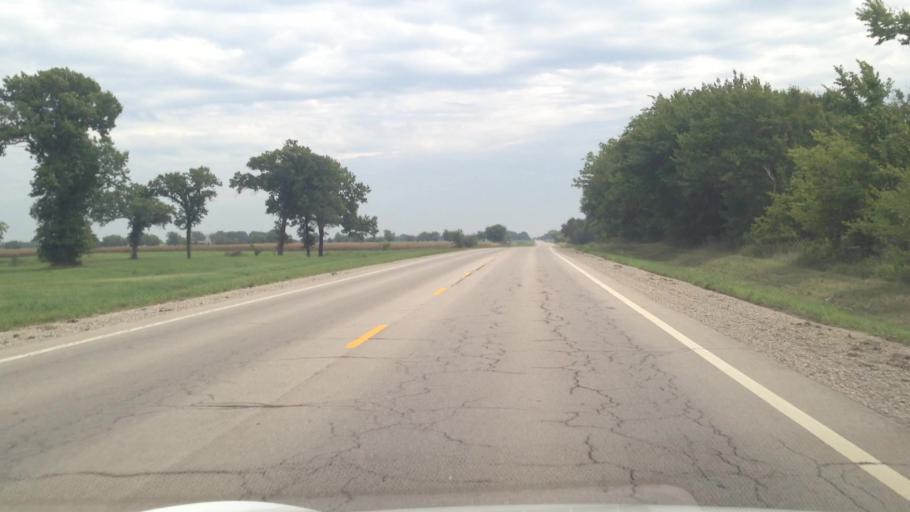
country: US
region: Kansas
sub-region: Crawford County
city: Girard
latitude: 37.5142
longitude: -94.8847
